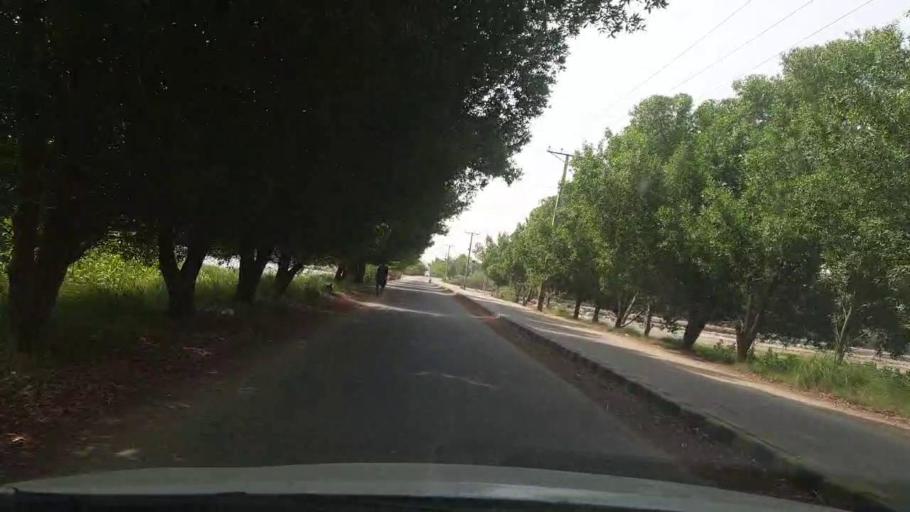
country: PK
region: Sindh
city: Kot Diji
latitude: 27.3511
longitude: 68.7120
